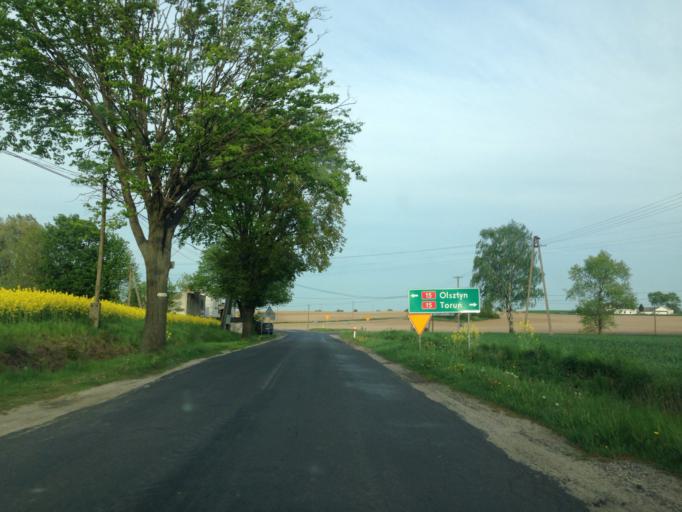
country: PL
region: Kujawsko-Pomorskie
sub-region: Powiat brodnicki
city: Bobrowo
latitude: 53.2263
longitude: 19.2027
